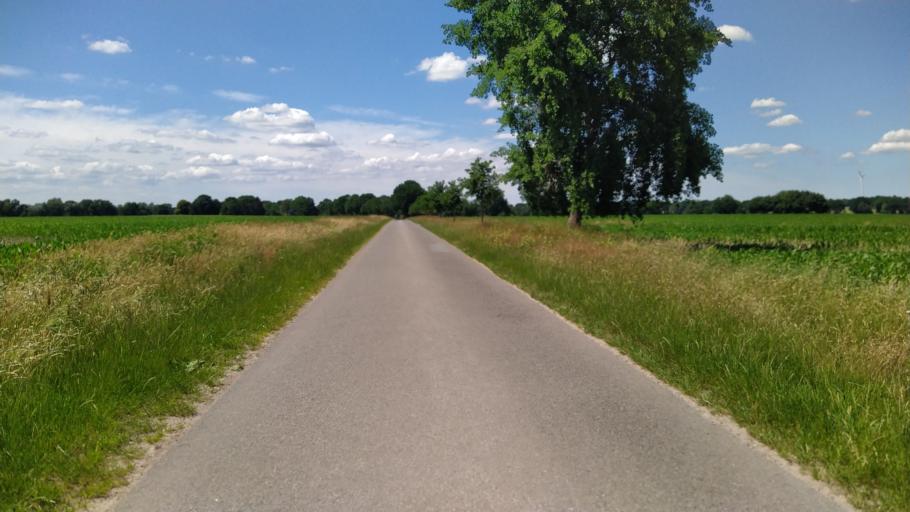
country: DE
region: Lower Saxony
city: Estorf
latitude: 53.5610
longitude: 9.2230
